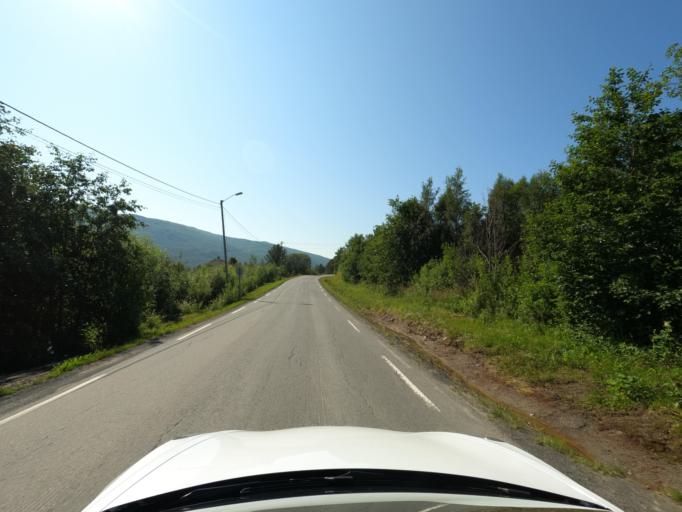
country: NO
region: Nordland
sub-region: Ballangen
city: Ballangen
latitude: 68.3520
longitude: 16.8613
